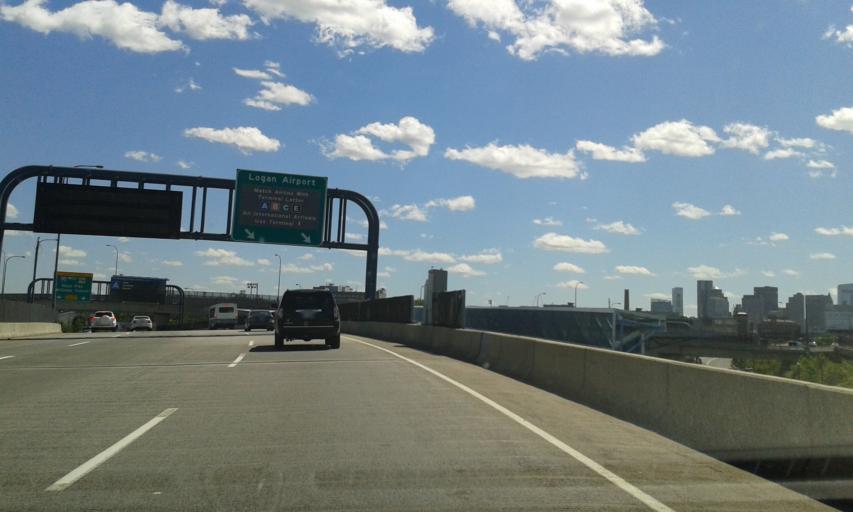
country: US
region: Massachusetts
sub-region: Suffolk County
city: Chelsea
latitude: 42.3755
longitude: -71.0296
